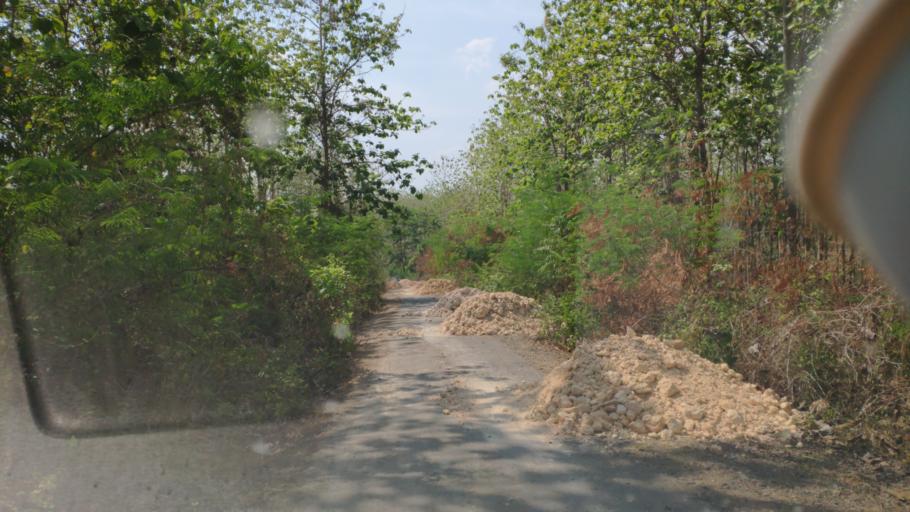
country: ID
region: Central Java
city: Balong Wetan
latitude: -6.9980
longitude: 111.2717
